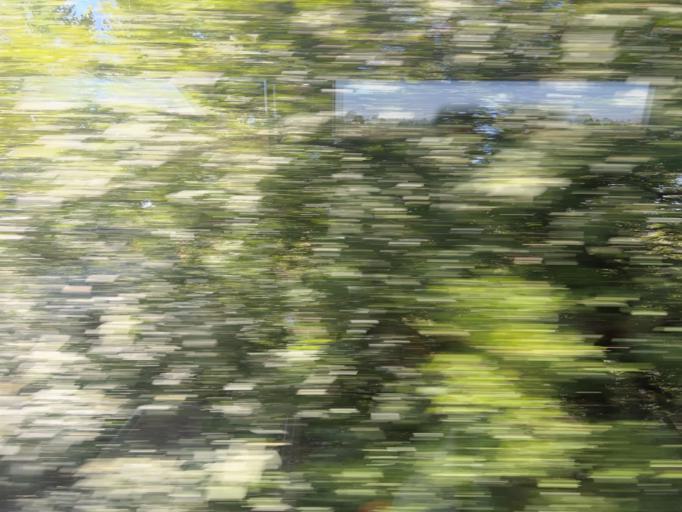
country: GB
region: England
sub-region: Lincolnshire
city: Sleaford
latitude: 52.9919
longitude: -0.3707
